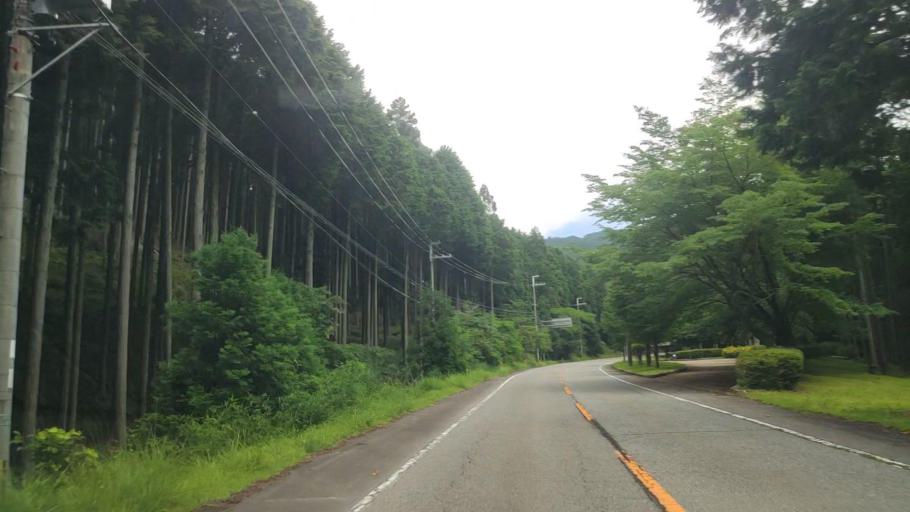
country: JP
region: Kyoto
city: Fukuchiyama
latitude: 35.2043
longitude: 134.9374
